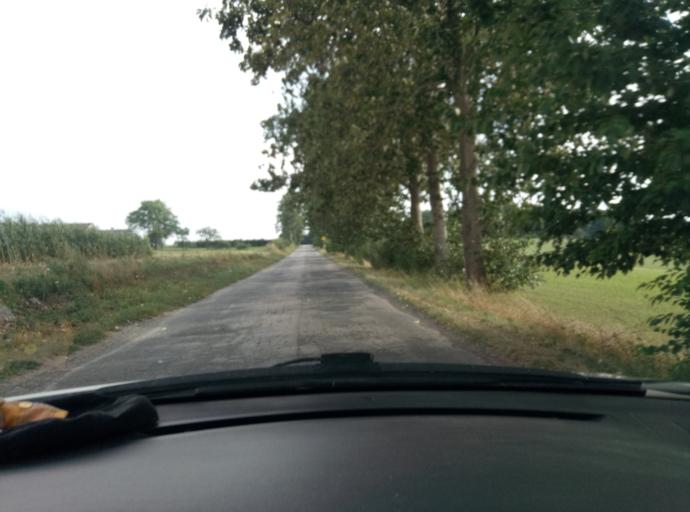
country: PL
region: Kujawsko-Pomorskie
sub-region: Powiat brodnicki
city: Jablonowo Pomorskie
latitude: 53.3770
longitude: 19.2449
